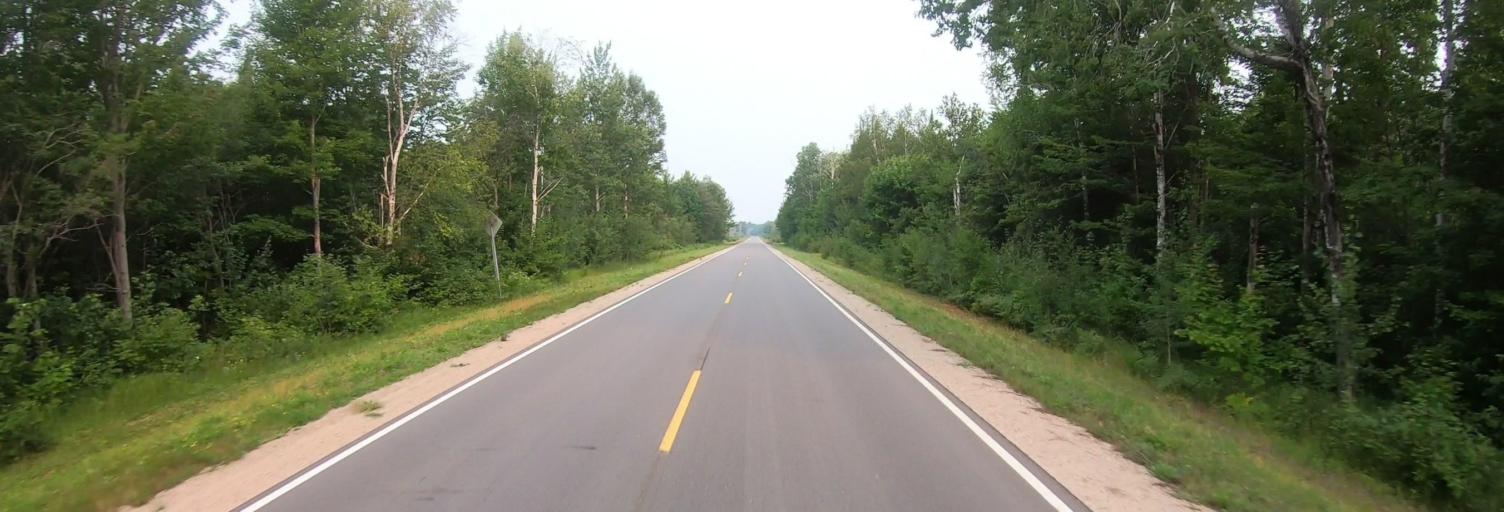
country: US
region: Michigan
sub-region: Luce County
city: Newberry
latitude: 46.4715
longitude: -84.9698
